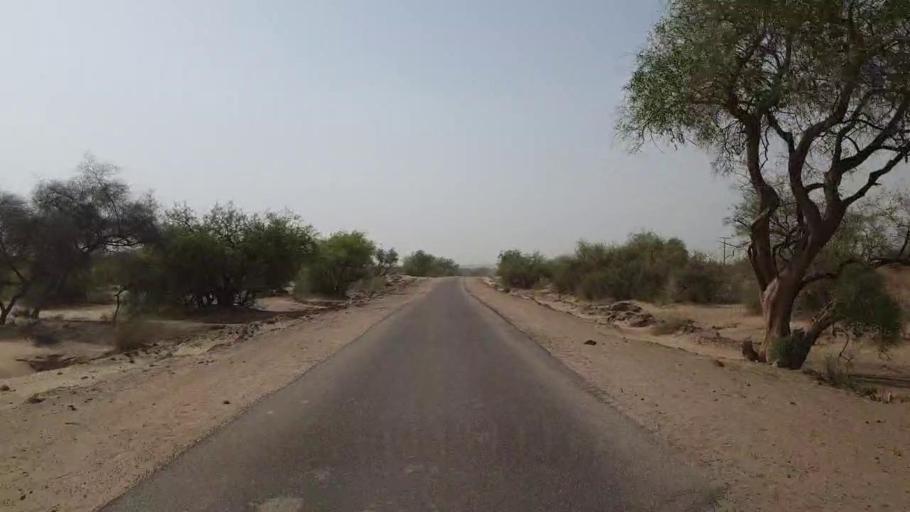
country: PK
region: Sindh
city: Mithi
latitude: 24.6041
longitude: 69.9222
